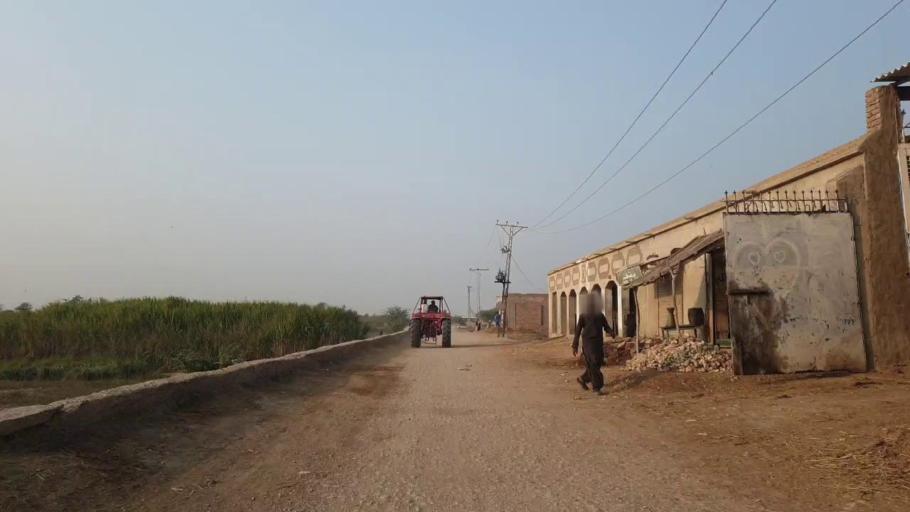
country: PK
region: Sindh
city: Tando Muhammad Khan
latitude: 25.0963
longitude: 68.4324
